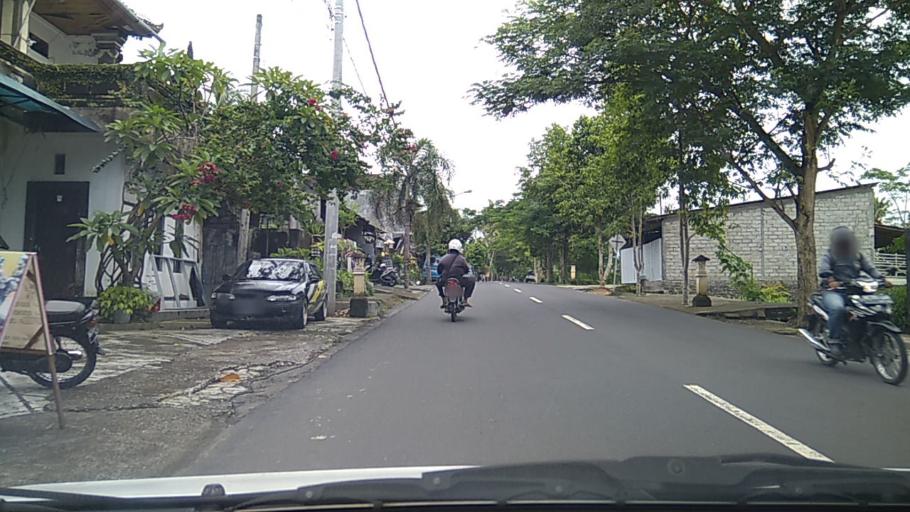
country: ID
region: Bali
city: Banjar Kelodan
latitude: -8.5168
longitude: 115.3457
